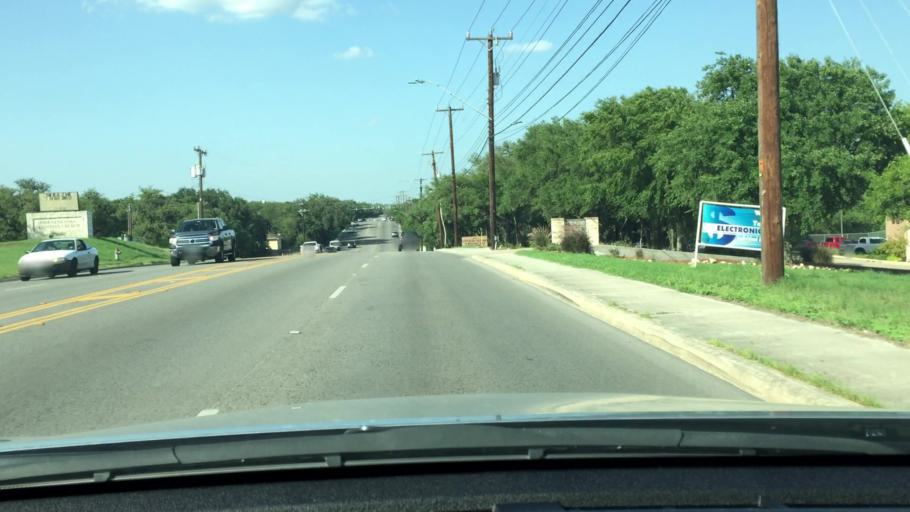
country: US
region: Texas
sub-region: Bexar County
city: Hollywood Park
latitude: 29.5596
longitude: -98.4608
